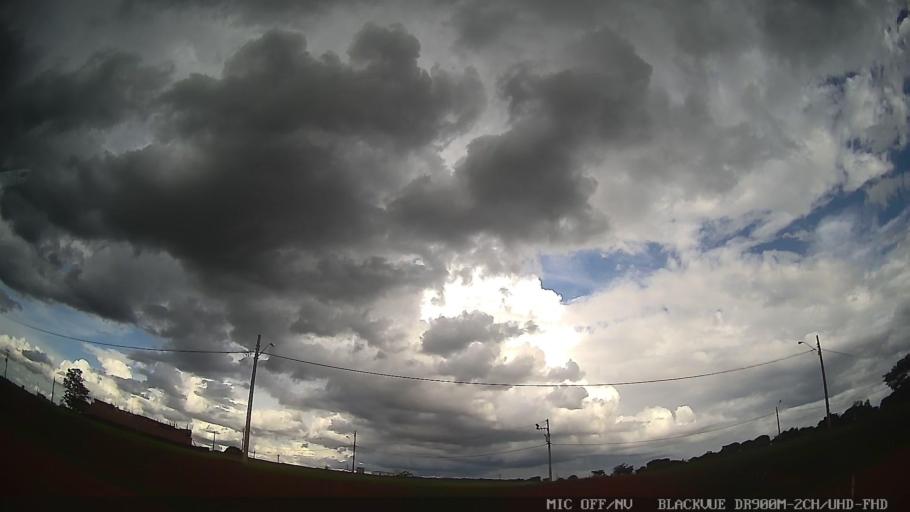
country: BR
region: Sao Paulo
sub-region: Jaguariuna
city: Jaguariuna
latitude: -22.6440
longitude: -47.0610
